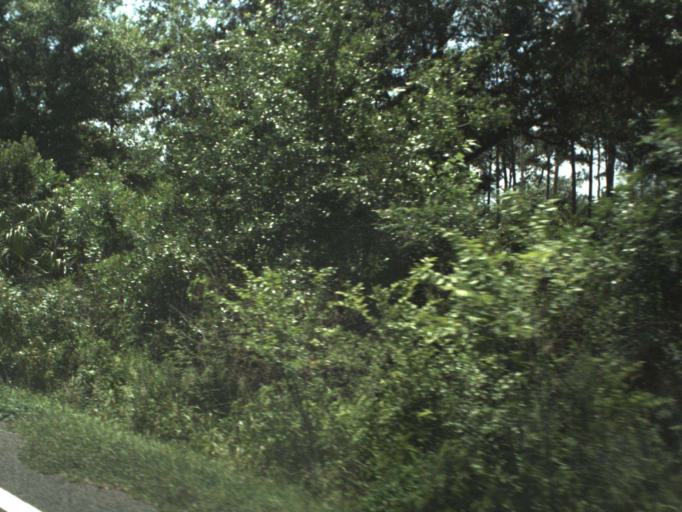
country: US
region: Florida
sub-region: Volusia County
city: Oak Hill
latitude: 28.8054
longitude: -80.8741
